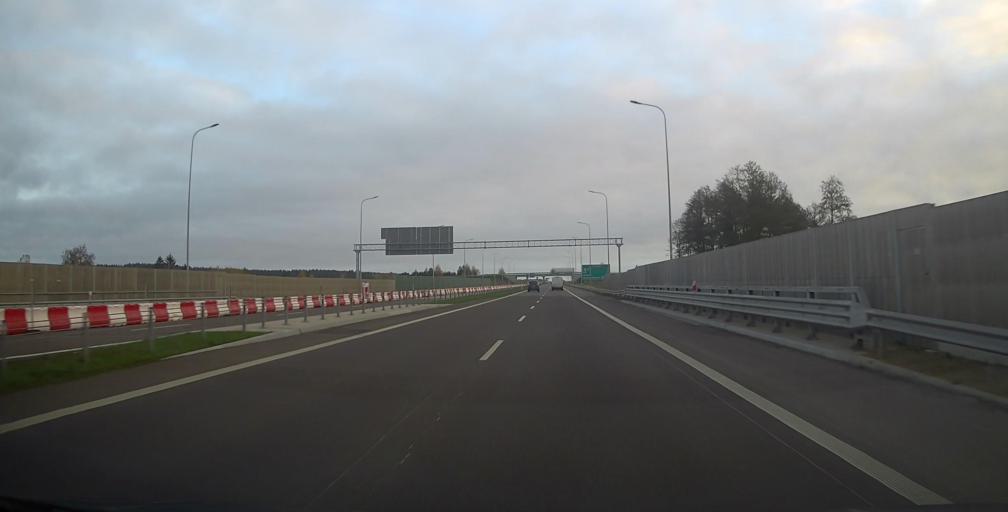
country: PL
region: Podlasie
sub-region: Powiat lomzynski
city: Piatnica
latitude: 53.2526
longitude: 22.1082
